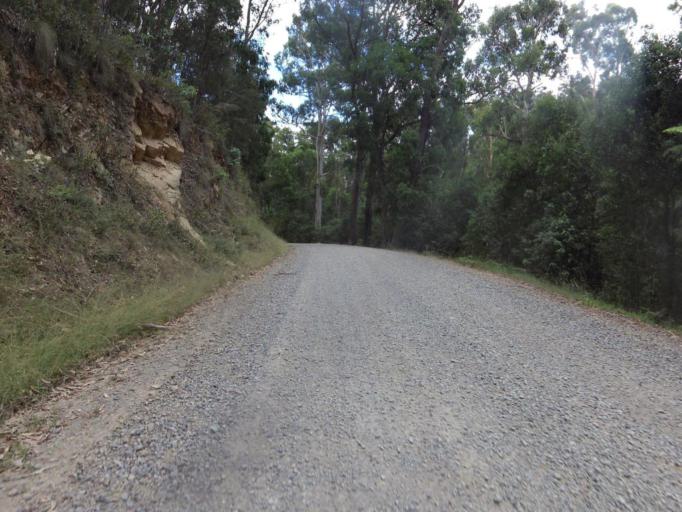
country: AU
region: Victoria
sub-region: Murrindindi
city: Alexandra
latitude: -37.3963
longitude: 145.5585
